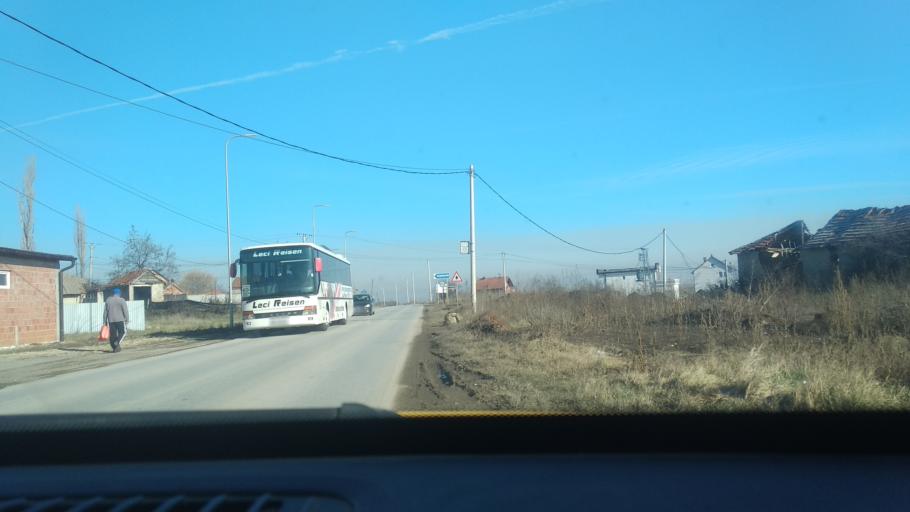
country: XK
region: Pristina
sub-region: Komuna e Gracanices
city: Glanica
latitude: 42.6031
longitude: 21.0273
